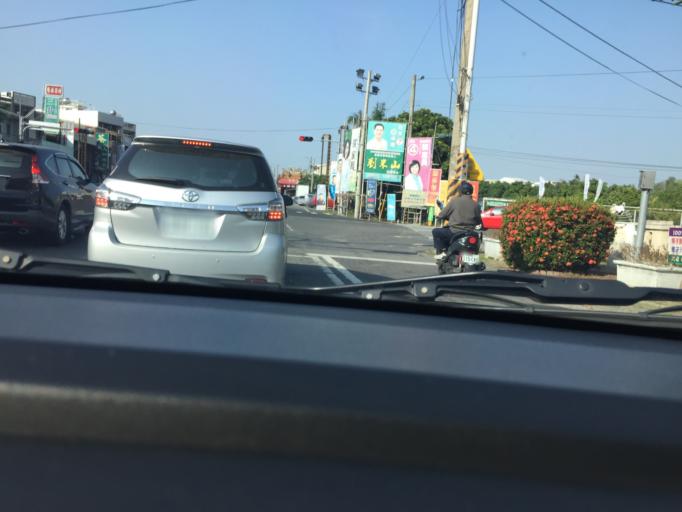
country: TW
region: Taiwan
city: Xinying
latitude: 23.2926
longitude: 120.3127
